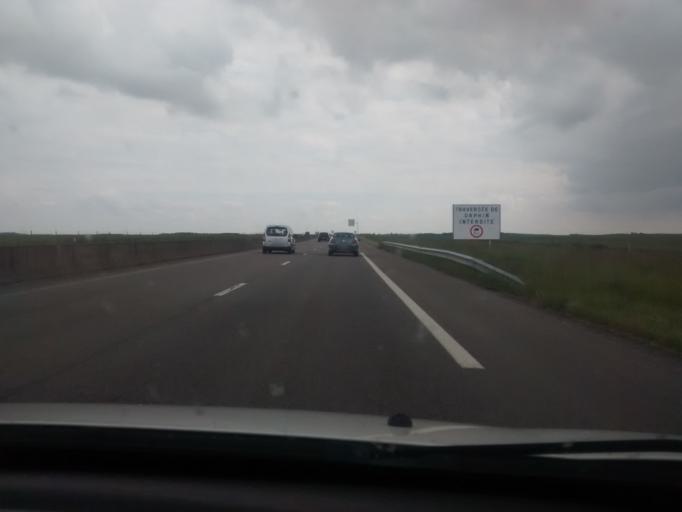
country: FR
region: Ile-de-France
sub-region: Departement des Yvelines
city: Sonchamp
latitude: 48.5862
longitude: 1.8320
